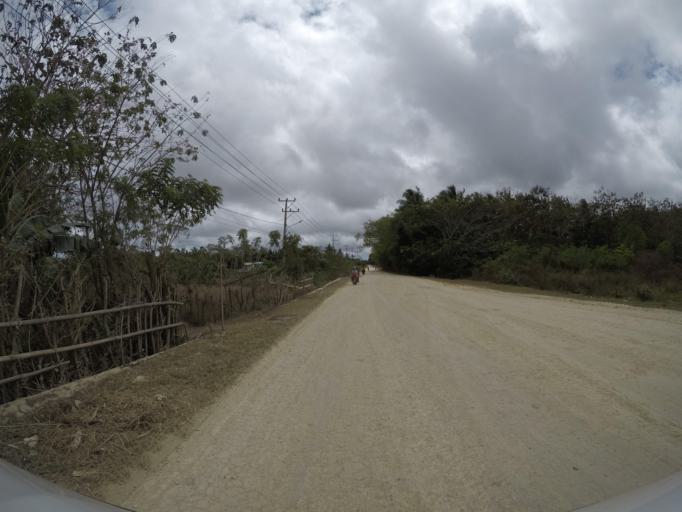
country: TL
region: Lautem
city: Lospalos
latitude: -8.4763
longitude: 126.9927
